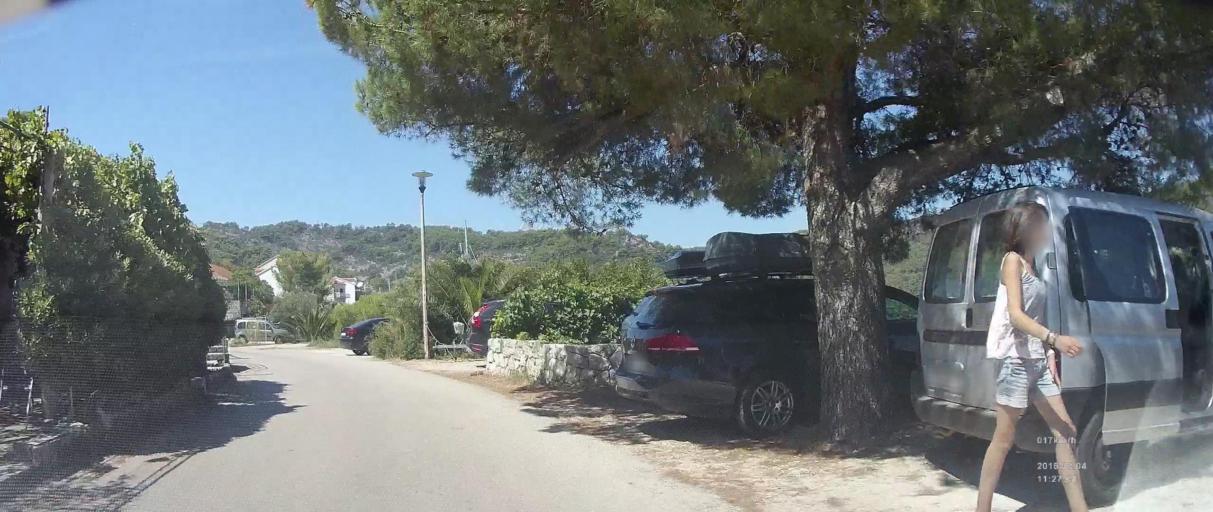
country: HR
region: Dubrovacko-Neretvanska
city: Blato
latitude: 42.7878
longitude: 17.3849
